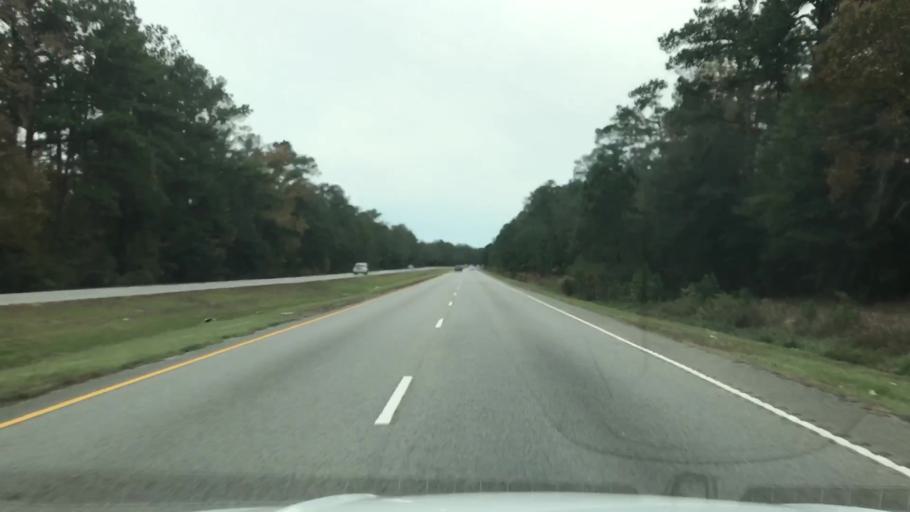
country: US
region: South Carolina
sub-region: Georgetown County
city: Georgetown
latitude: 33.3904
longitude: -79.2039
